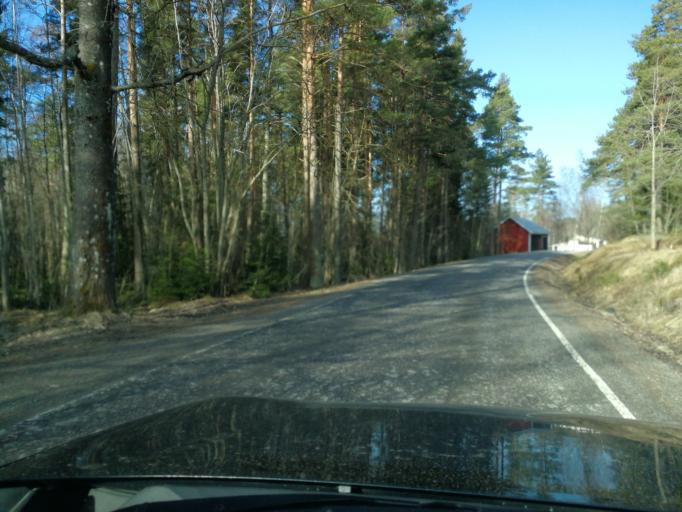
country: FI
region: Uusimaa
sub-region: Raaseporin
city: Inga
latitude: 60.0497
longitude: 24.0358
